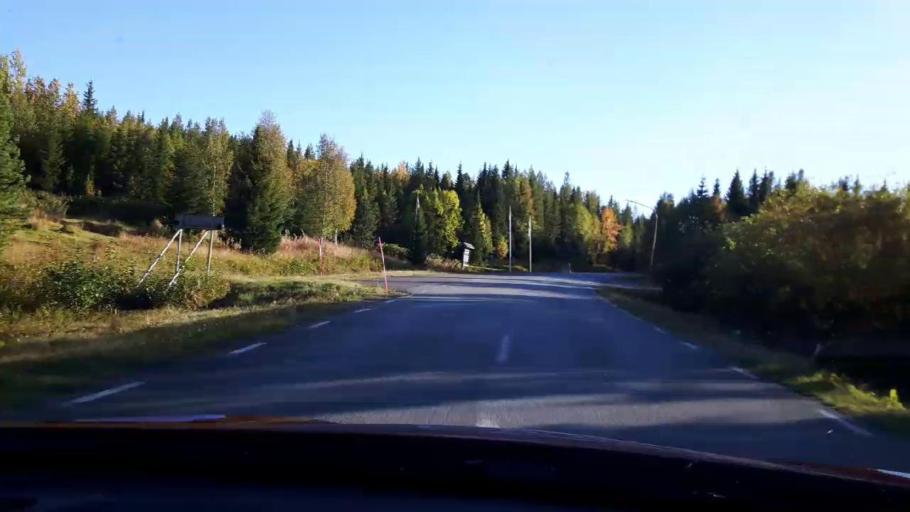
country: SE
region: Jaemtland
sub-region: OEstersunds Kommun
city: Lit
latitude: 63.7982
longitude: 14.7097
